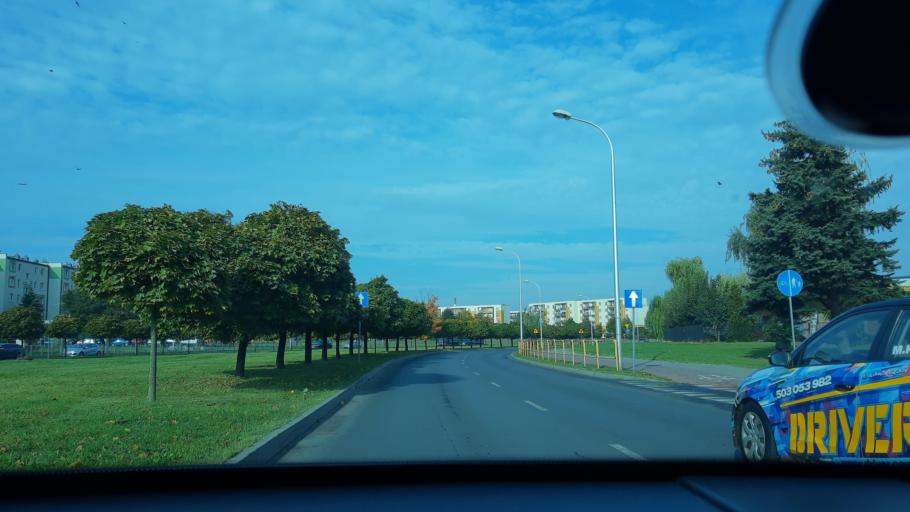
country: PL
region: Lodz Voivodeship
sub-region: Powiat sieradzki
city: Sieradz
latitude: 51.5900
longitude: 18.7167
